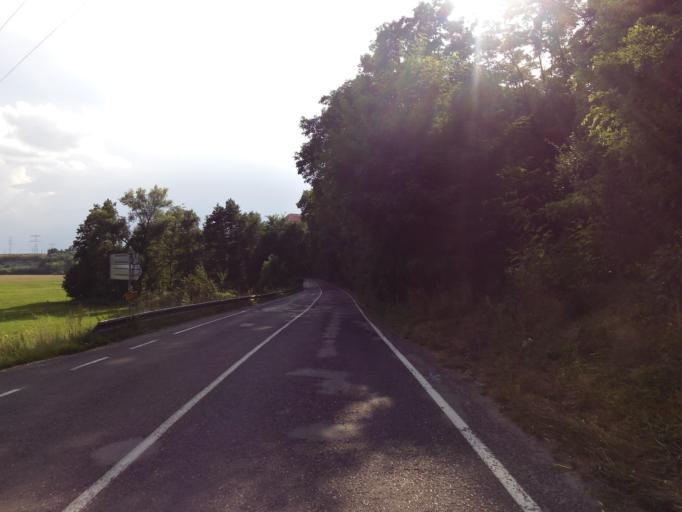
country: CZ
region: Central Bohemia
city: Mnichovo Hradiste
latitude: 50.5263
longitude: 14.9520
